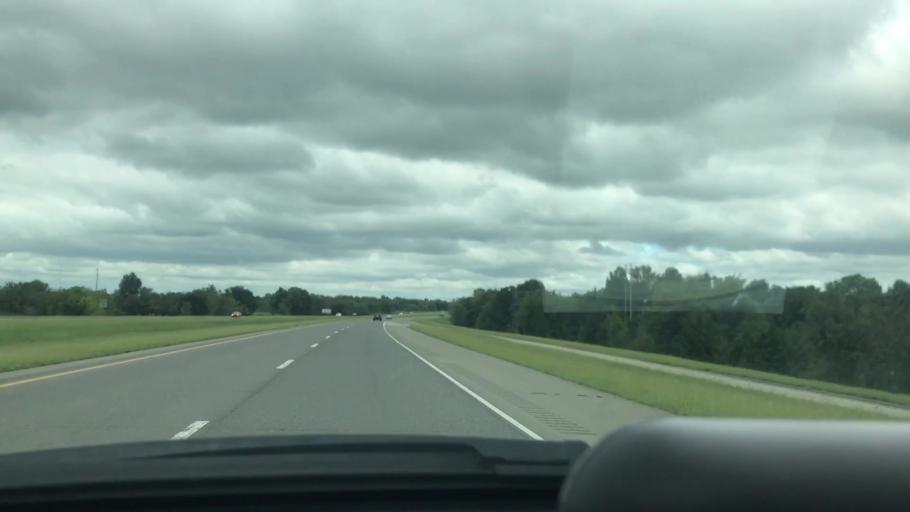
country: US
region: Oklahoma
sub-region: McIntosh County
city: Checotah
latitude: 35.5784
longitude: -95.4907
